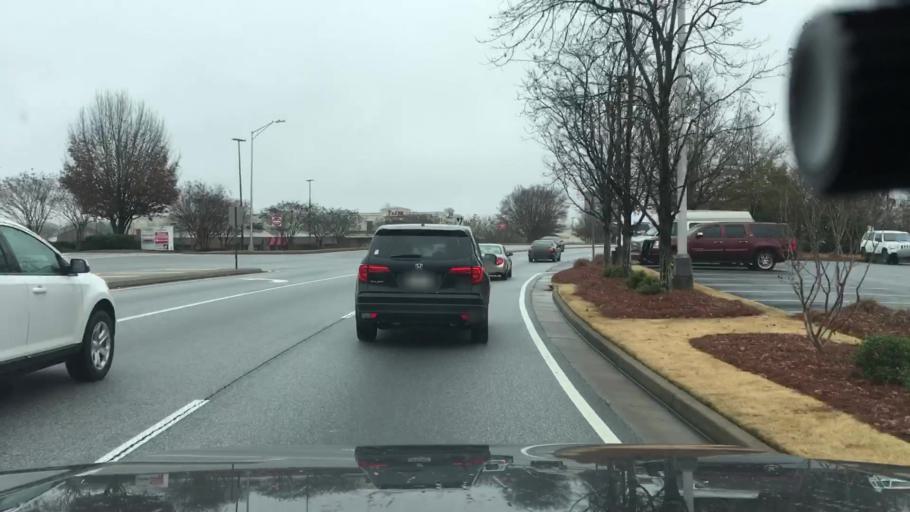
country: US
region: Georgia
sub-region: Coweta County
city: Newnan
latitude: 33.3944
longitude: -84.7613
